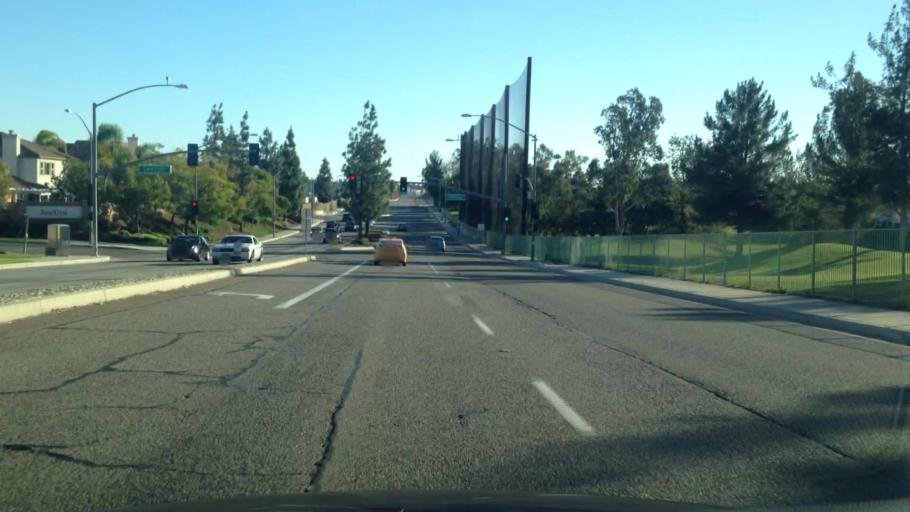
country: US
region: California
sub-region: Orange County
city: Placentia
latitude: 33.8729
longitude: -117.8431
